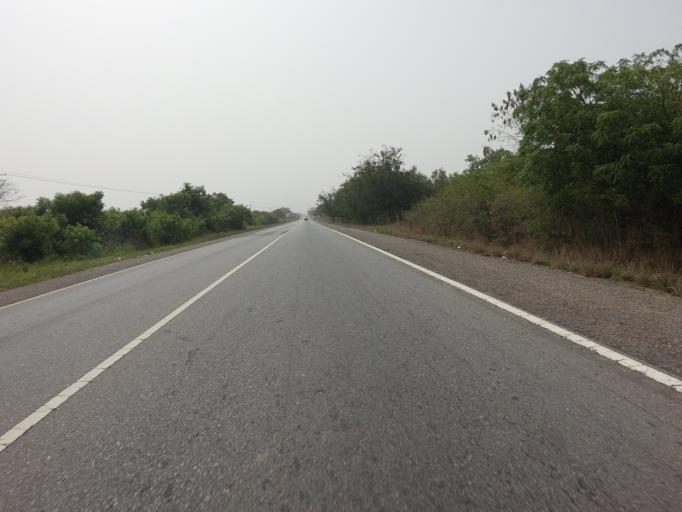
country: GH
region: Volta
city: Anloga
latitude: 5.9578
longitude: 0.5242
